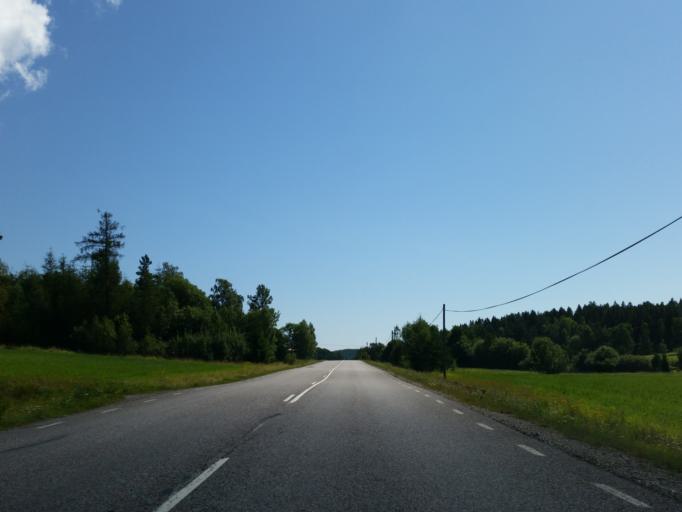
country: SE
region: Soedermanland
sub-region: Trosa Kommun
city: Vagnharad
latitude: 58.9977
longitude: 17.6088
